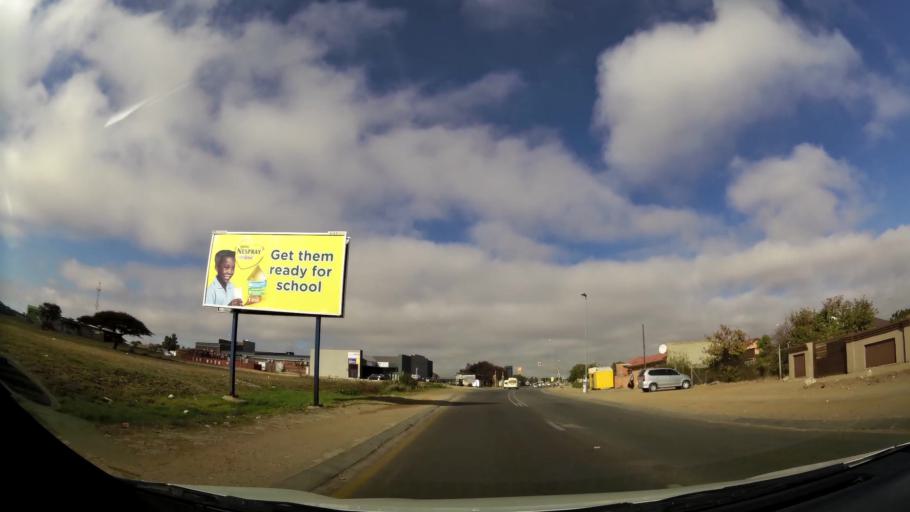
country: ZA
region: Limpopo
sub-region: Capricorn District Municipality
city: Polokwane
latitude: -23.8501
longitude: 29.3789
